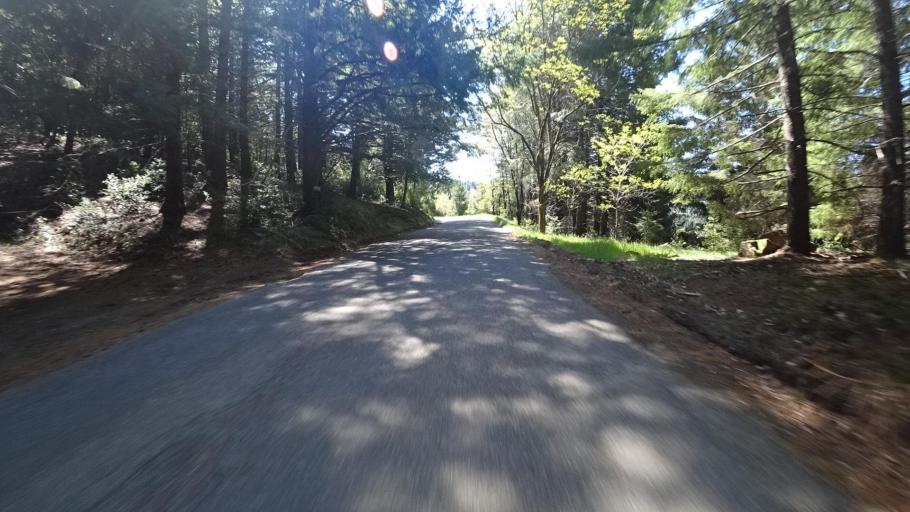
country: US
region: California
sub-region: Humboldt County
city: Redway
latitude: 40.1158
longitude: -123.9667
